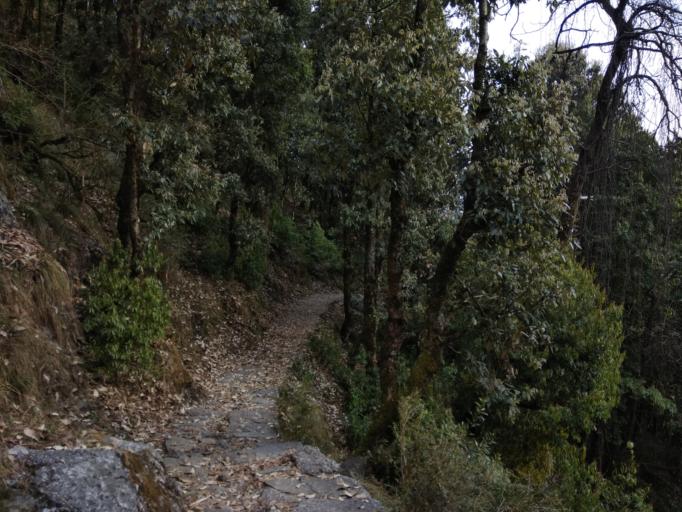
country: IN
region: Himachal Pradesh
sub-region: Kangra
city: Dharmsala
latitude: 32.2713
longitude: 76.3144
